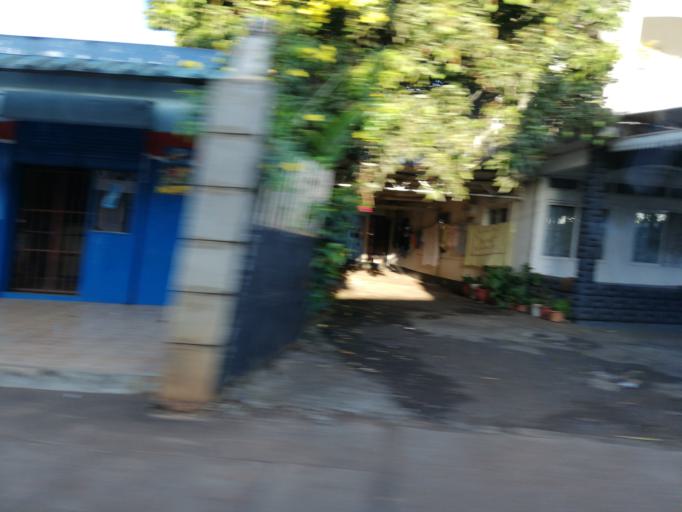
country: MU
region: Pamplemousses
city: Terre Rouge
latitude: -20.1221
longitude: 57.5316
